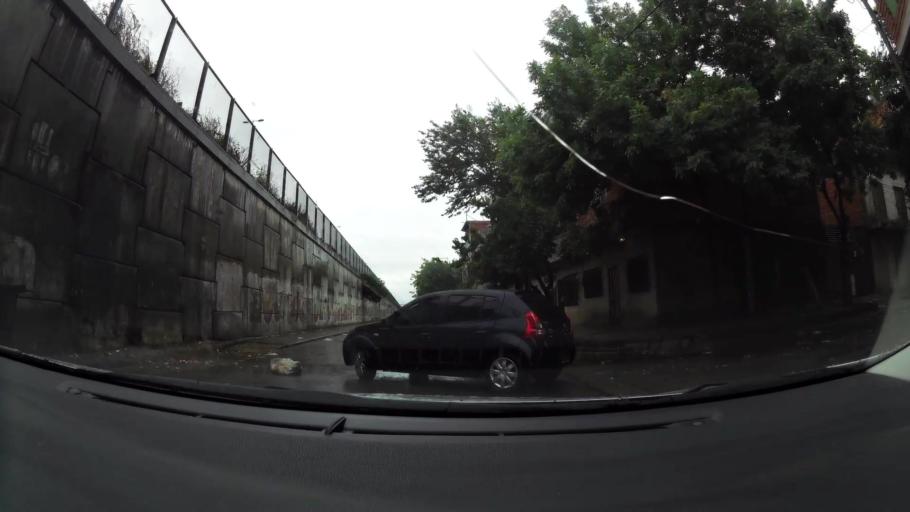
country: AR
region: Buenos Aires F.D.
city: Villa Lugano
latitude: -34.6619
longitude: -58.4536
